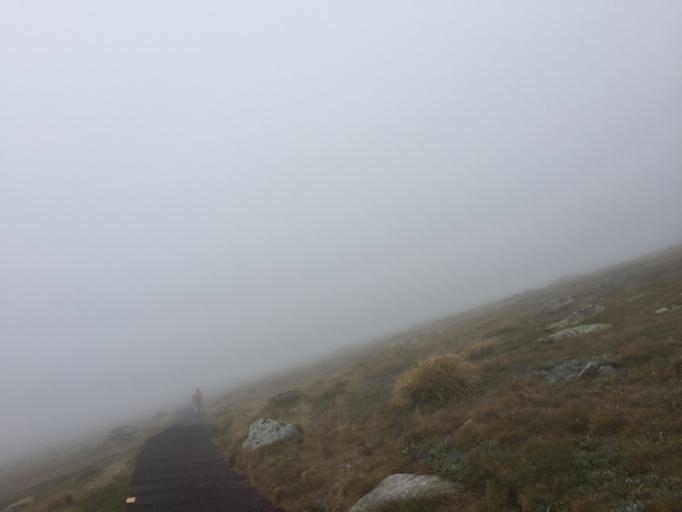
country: AU
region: New South Wales
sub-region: Snowy River
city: Jindabyne
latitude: -36.4598
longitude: 148.2702
